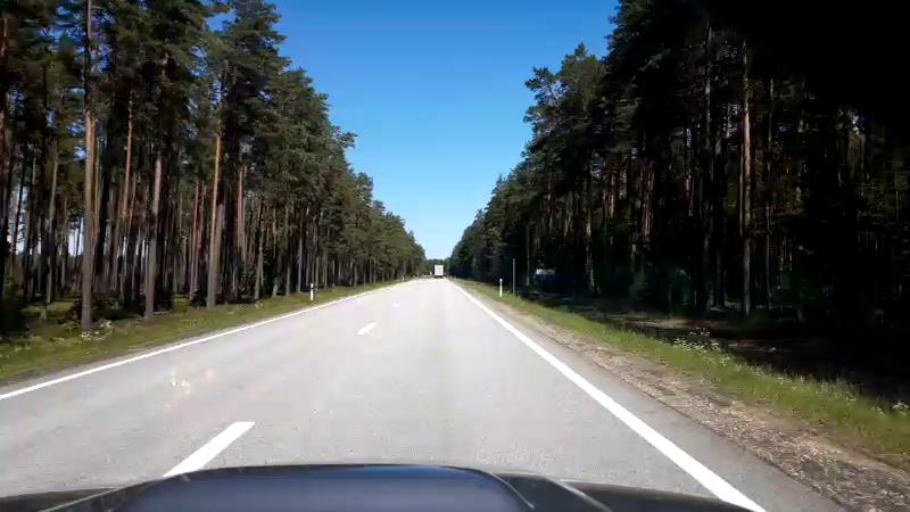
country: LV
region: Salacgrivas
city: Salacgriva
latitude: 57.5647
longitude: 24.4342
